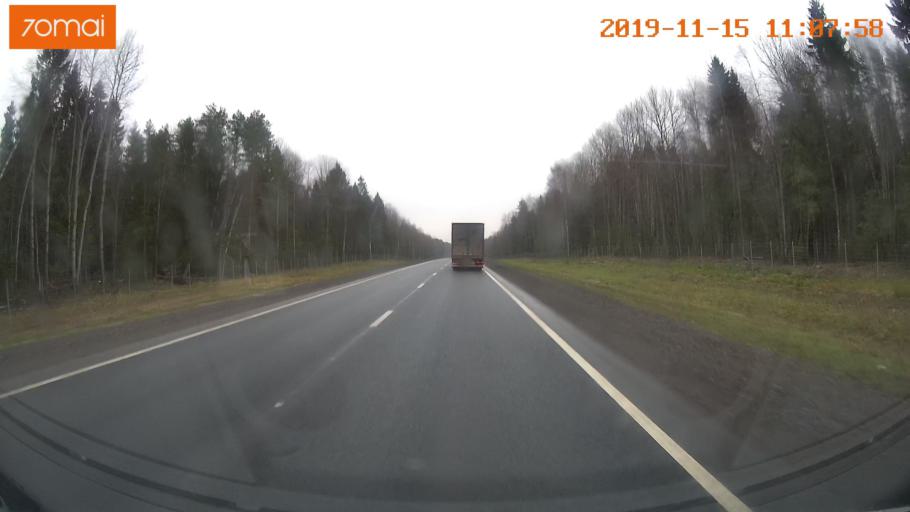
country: RU
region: Vologda
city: Chebsara
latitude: 59.1197
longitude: 39.0630
